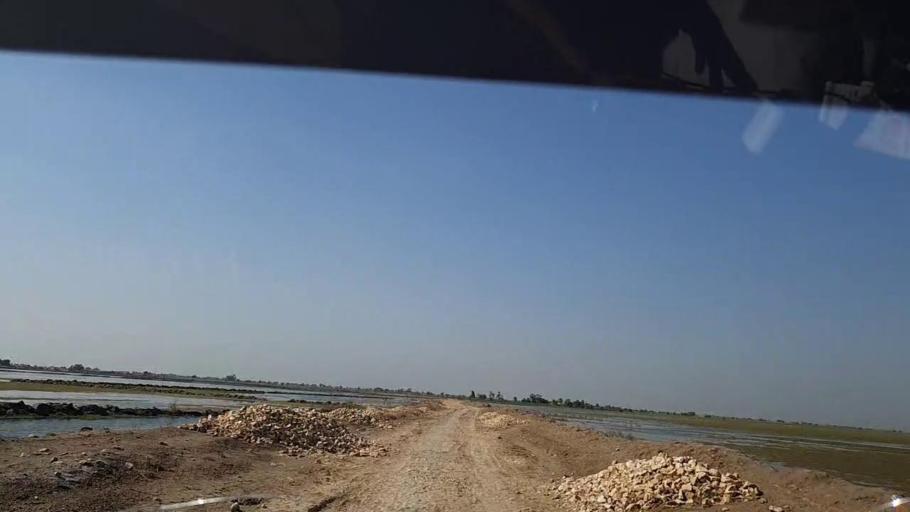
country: PK
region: Sindh
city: Tangwani
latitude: 28.3568
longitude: 69.0379
